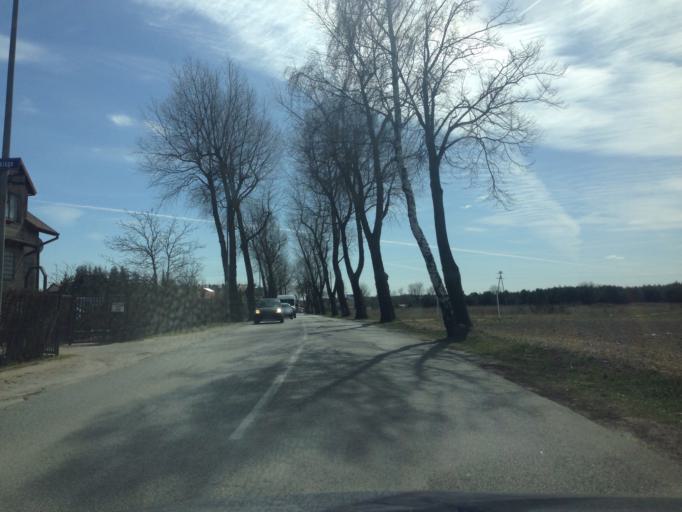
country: PL
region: Pomeranian Voivodeship
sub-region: Powiat wejherowski
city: Bojano
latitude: 54.4968
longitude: 18.4307
